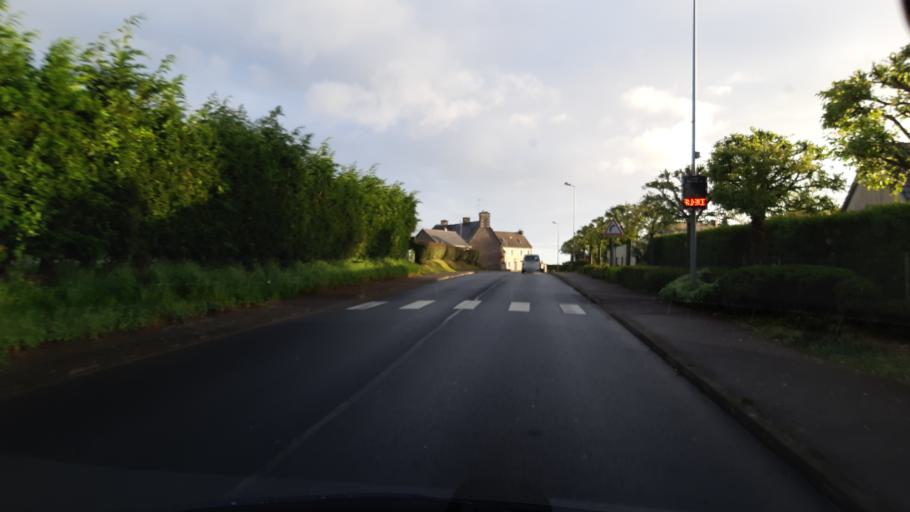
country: FR
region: Lower Normandy
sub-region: Departement de la Manche
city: Tessy-sur-Vire
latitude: 49.0265
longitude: -1.1450
